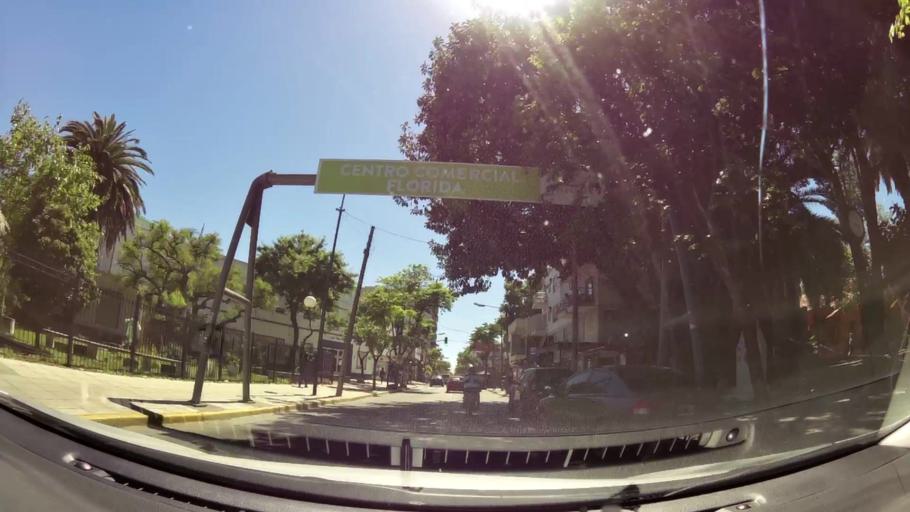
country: AR
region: Buenos Aires
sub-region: Partido de Vicente Lopez
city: Olivos
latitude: -34.5291
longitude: -58.4943
